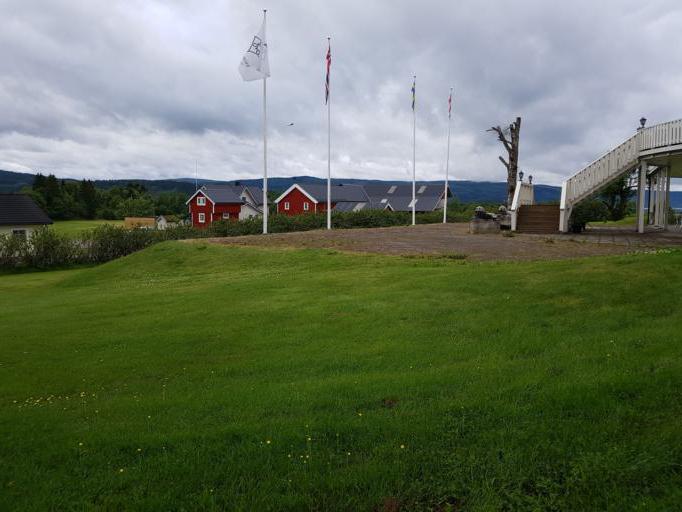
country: NO
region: Sor-Trondelag
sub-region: Selbu
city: Mebonden
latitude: 63.2323
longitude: 11.0303
